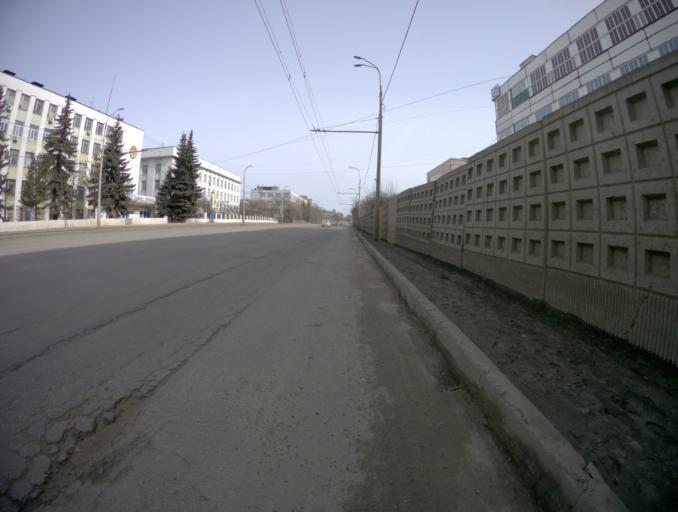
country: RU
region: Vladimir
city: Kommunar
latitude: 56.1449
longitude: 40.4432
